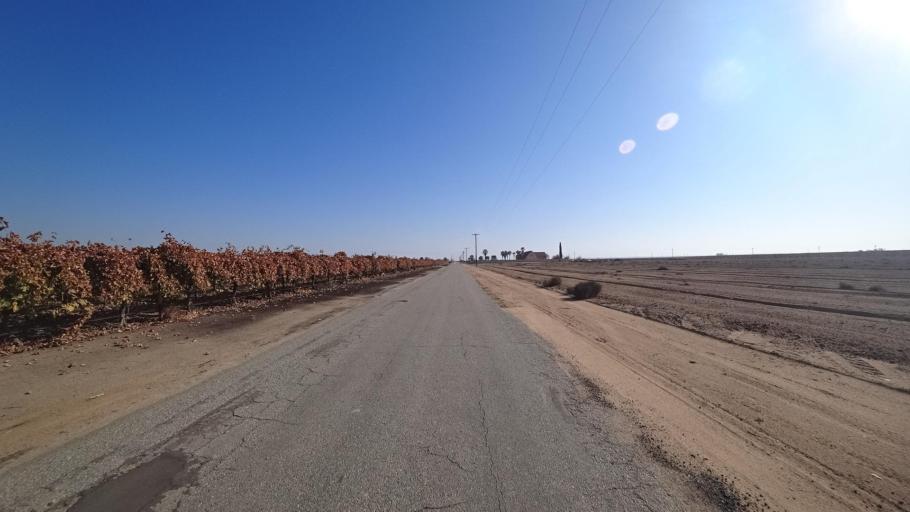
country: US
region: California
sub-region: Kern County
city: Delano
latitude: 35.7397
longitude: -119.2179
